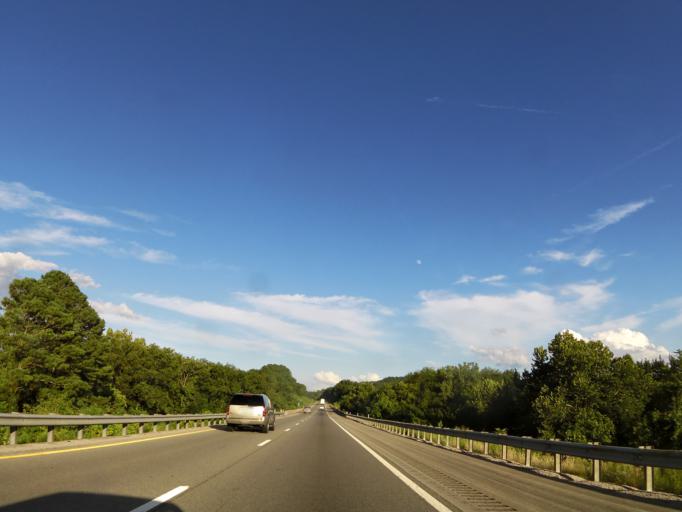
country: US
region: Tennessee
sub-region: Smith County
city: Gordonsville
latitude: 36.1701
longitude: -85.9113
